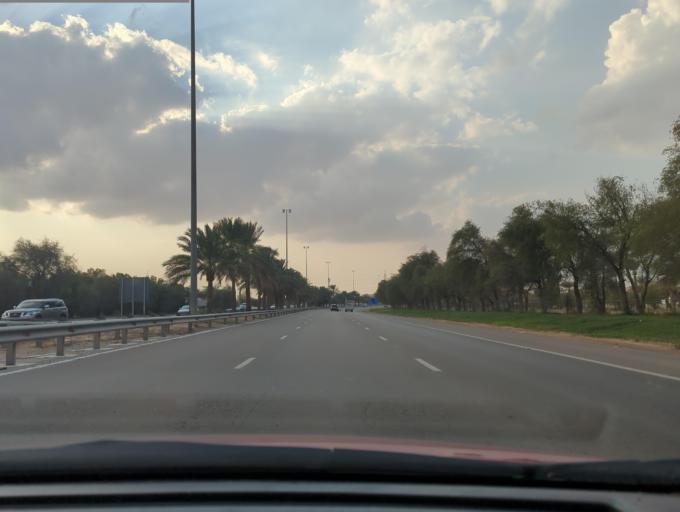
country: AE
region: Abu Dhabi
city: Al Ain
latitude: 24.2017
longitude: 55.5733
